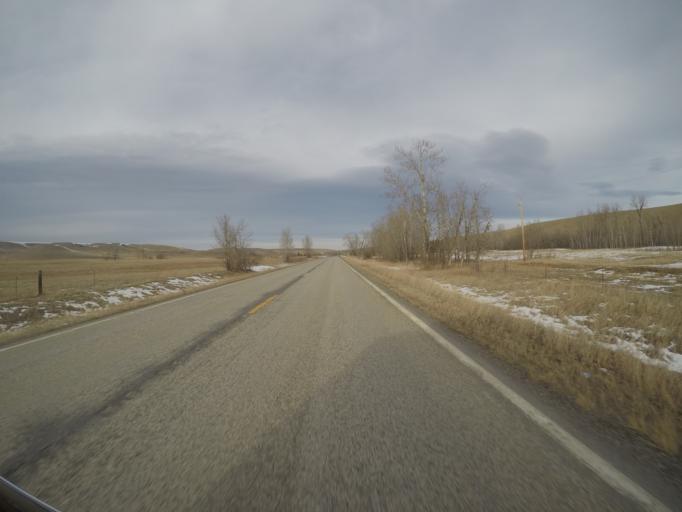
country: US
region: Montana
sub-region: Stillwater County
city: Absarokee
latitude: 45.4189
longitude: -109.4726
